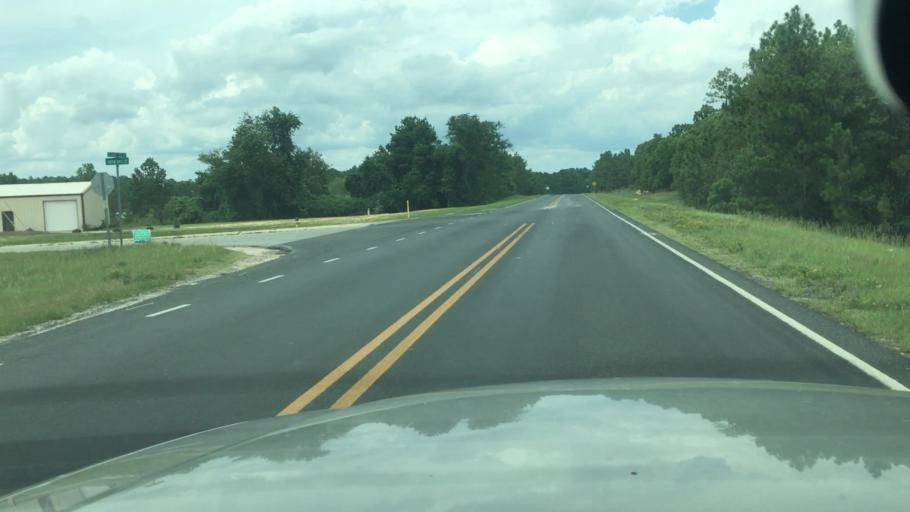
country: US
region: North Carolina
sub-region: Cumberland County
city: Hope Mills
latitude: 34.9712
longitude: -78.8933
